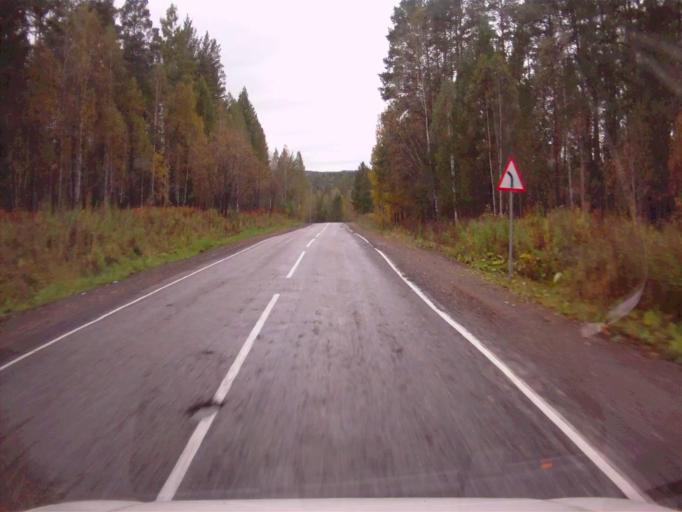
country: RU
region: Chelyabinsk
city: Nyazepetrovsk
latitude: 56.0628
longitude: 59.7265
